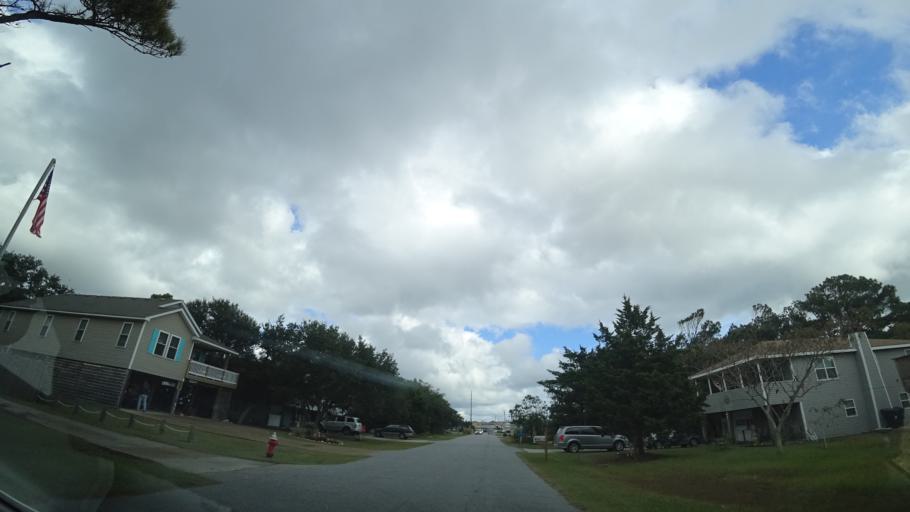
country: US
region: North Carolina
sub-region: Dare County
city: Kill Devil Hills
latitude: 35.9964
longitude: -75.6536
